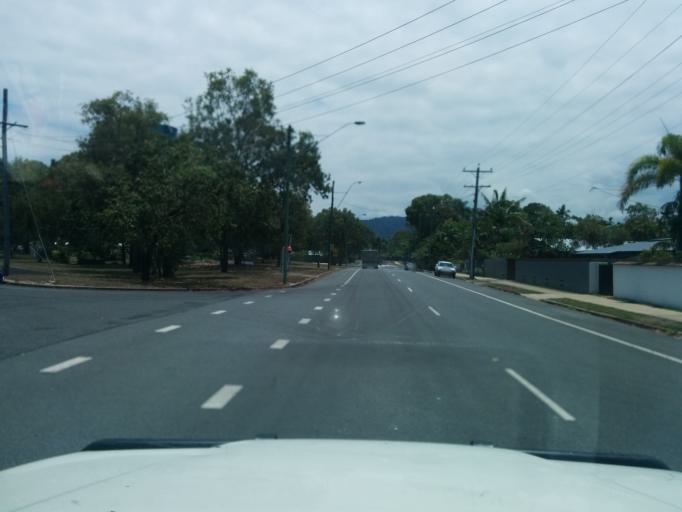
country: AU
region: Queensland
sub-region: Cairns
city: Yorkeys Knob
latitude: -16.8408
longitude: 145.7397
